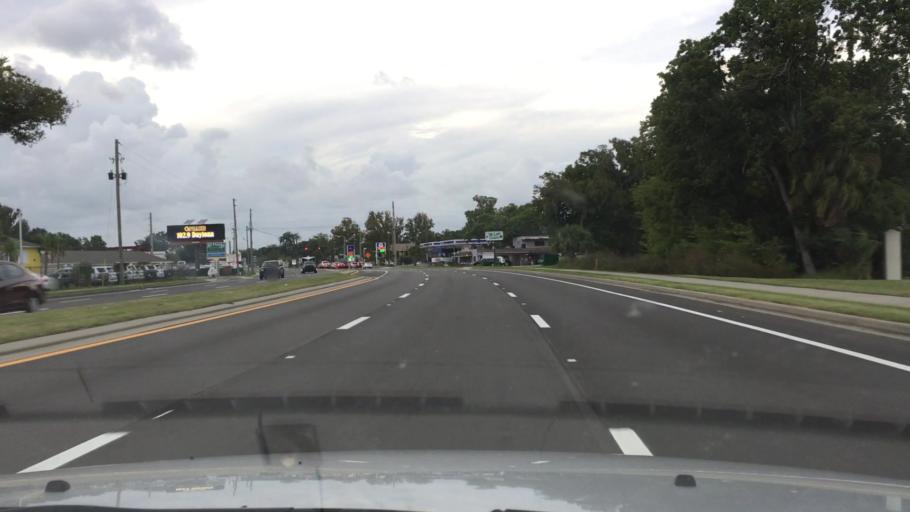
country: US
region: Florida
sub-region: Volusia County
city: Holly Hill
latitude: 29.2401
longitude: -81.0584
